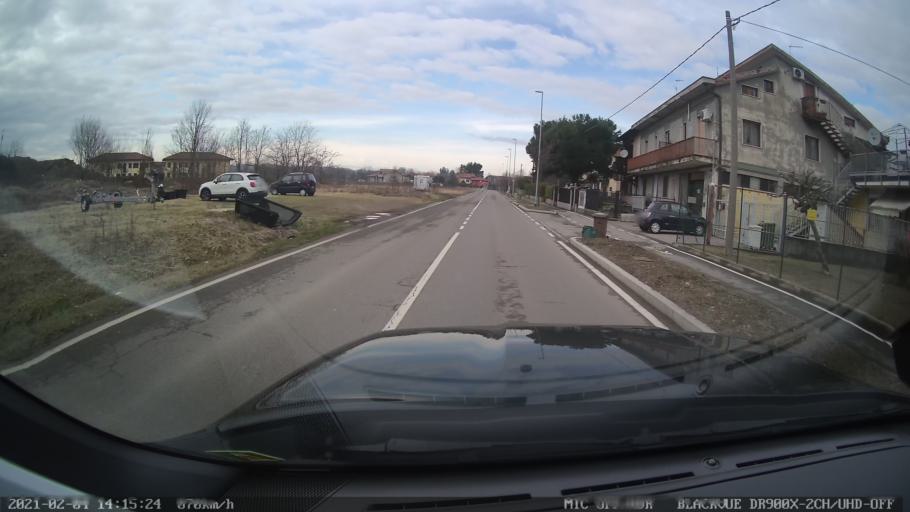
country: IT
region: Lombardy
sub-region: Provincia di Varese
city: Lonate Ceppino
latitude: 45.7235
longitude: 8.8849
